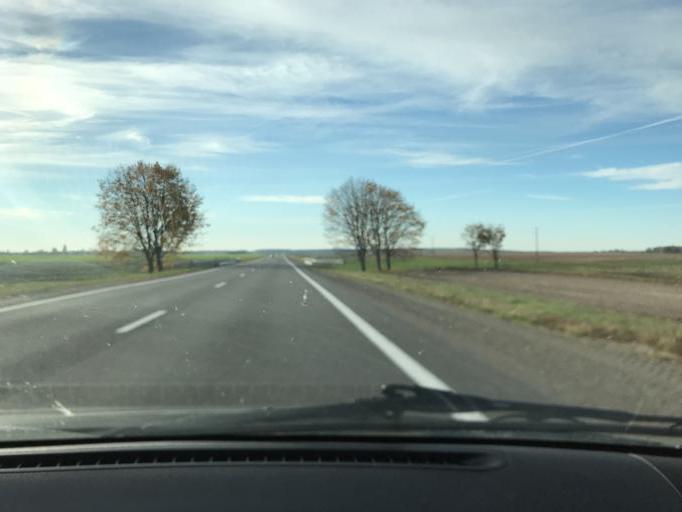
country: BY
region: Brest
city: Ivanava
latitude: 52.1560
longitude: 25.6671
